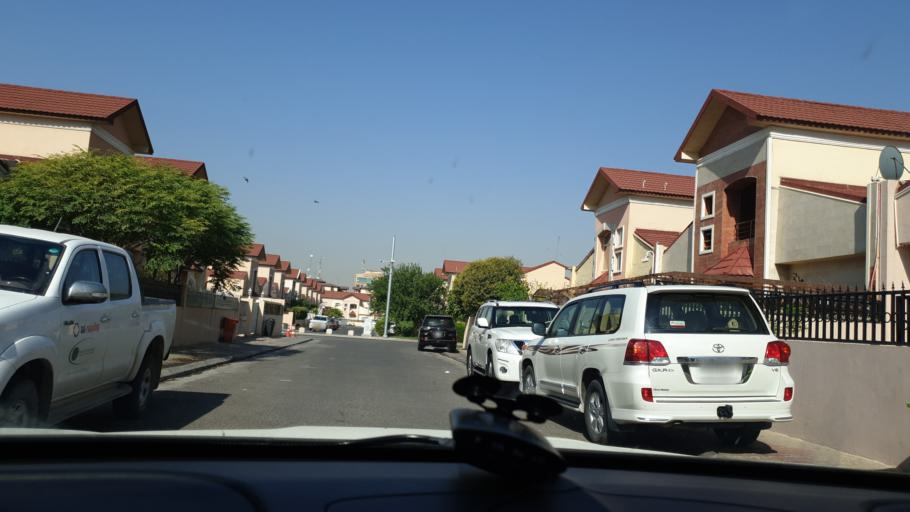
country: IQ
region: Arbil
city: Erbil
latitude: 36.1866
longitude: 43.9673
